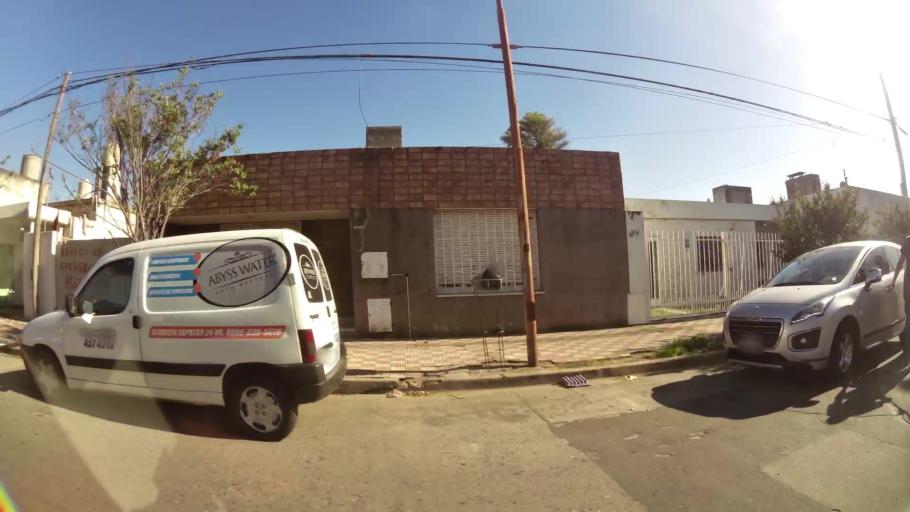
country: AR
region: Cordoba
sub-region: Departamento de Capital
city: Cordoba
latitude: -31.4253
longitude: -64.1630
